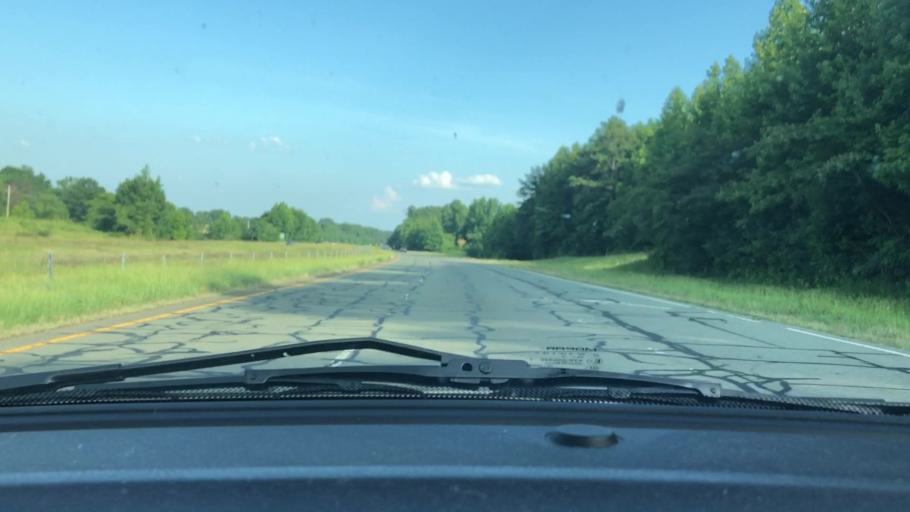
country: US
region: North Carolina
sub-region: Chatham County
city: Siler City
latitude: 35.6898
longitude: -79.4252
